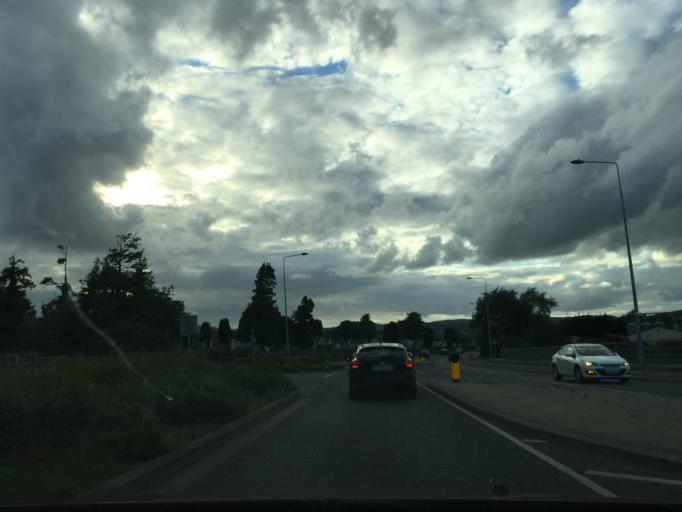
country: IE
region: Leinster
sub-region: Wicklow
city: Rathnew
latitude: 52.9924
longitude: -6.0734
